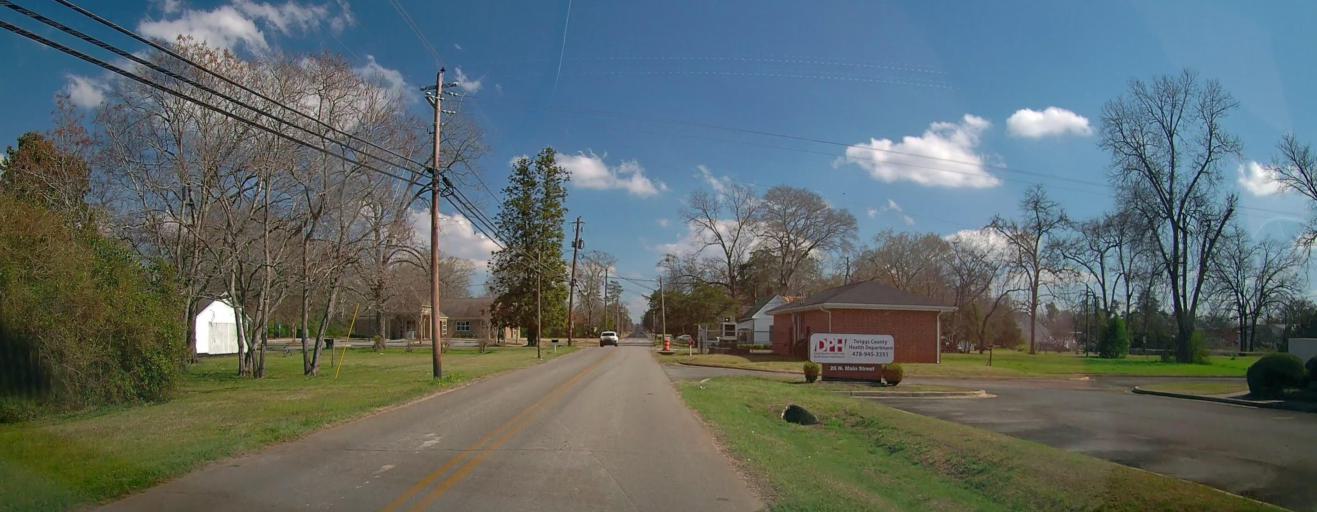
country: US
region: Georgia
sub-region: Twiggs County
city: Jeffersonville
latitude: 32.6889
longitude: -83.3442
